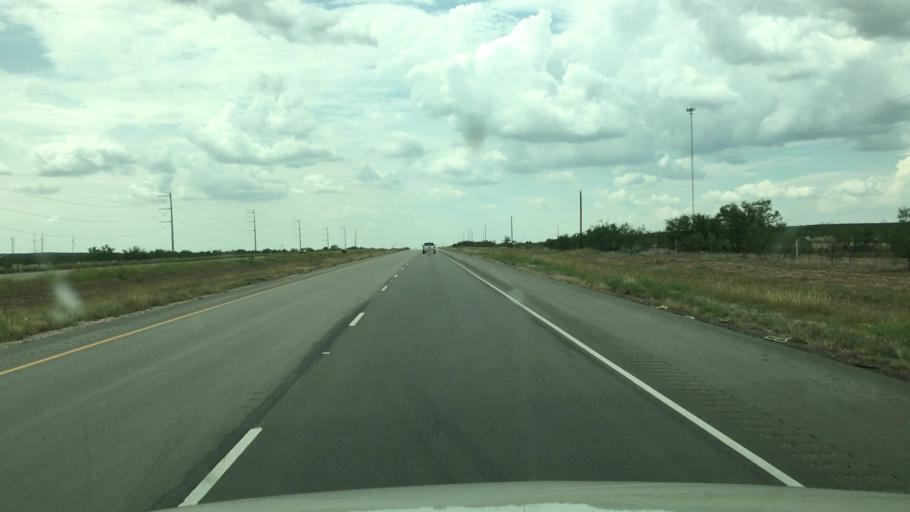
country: US
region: Texas
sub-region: Glasscock County
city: Garden City
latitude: 31.9768
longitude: -101.2498
